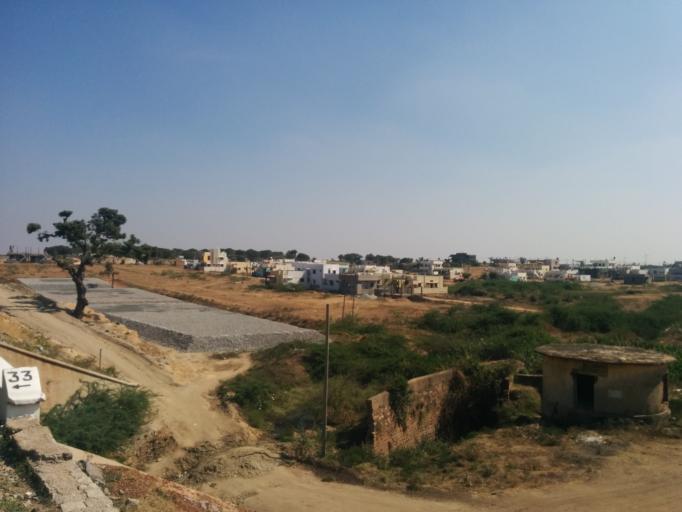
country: IN
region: Karnataka
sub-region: Gadag
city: Gadag
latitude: 15.4379
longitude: 75.6574
